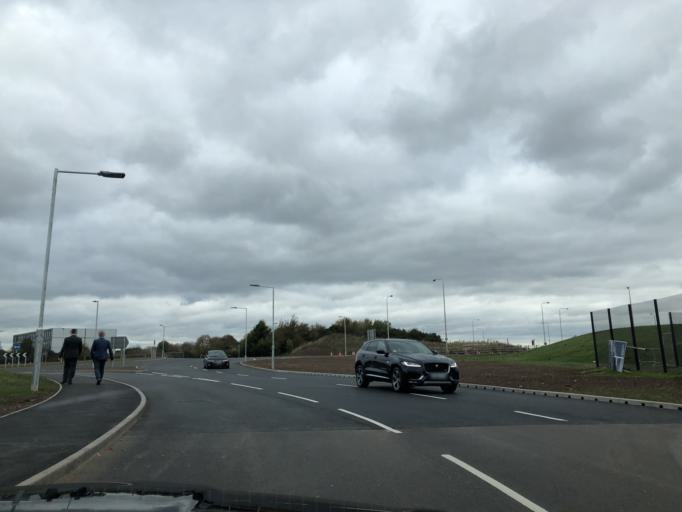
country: GB
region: England
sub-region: Warwickshire
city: Harbury
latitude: 52.1900
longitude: -1.4753
